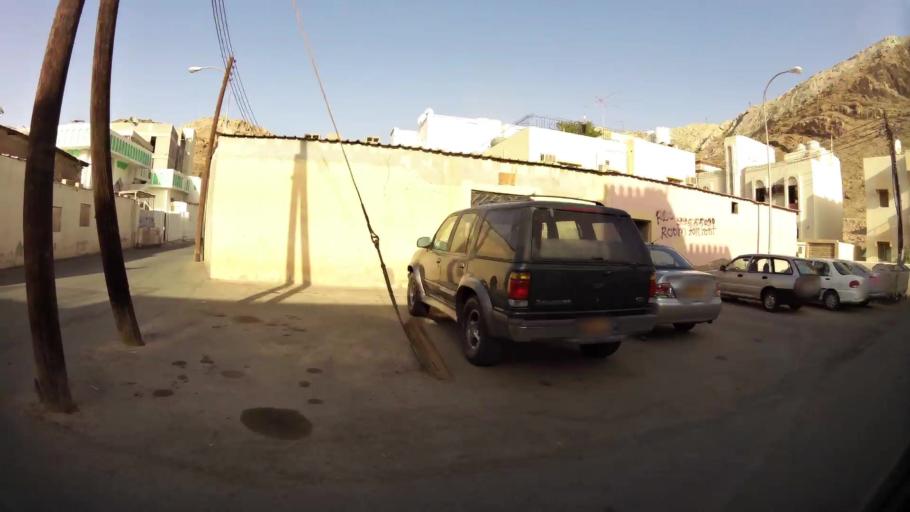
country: OM
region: Muhafazat Masqat
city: Muscat
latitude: 23.5838
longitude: 58.5508
